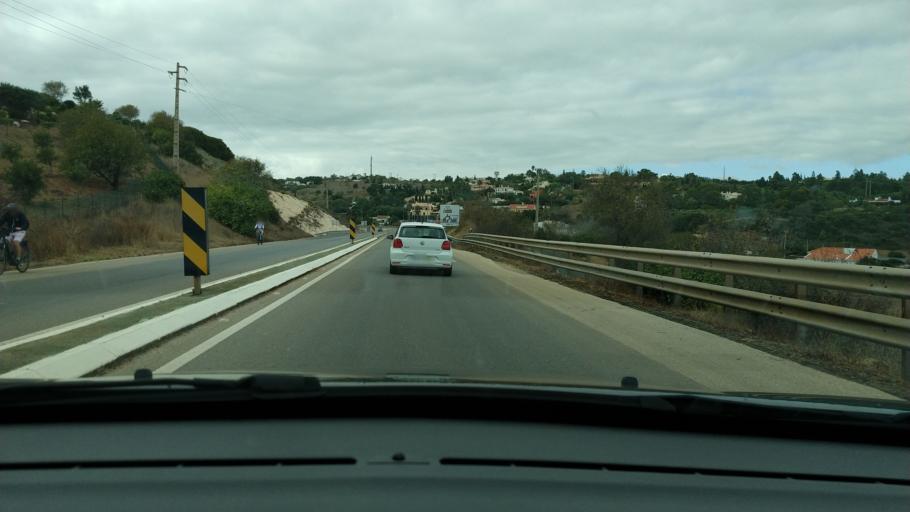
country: PT
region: Faro
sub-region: Lagos
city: Lagos
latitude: 37.1051
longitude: -8.7041
